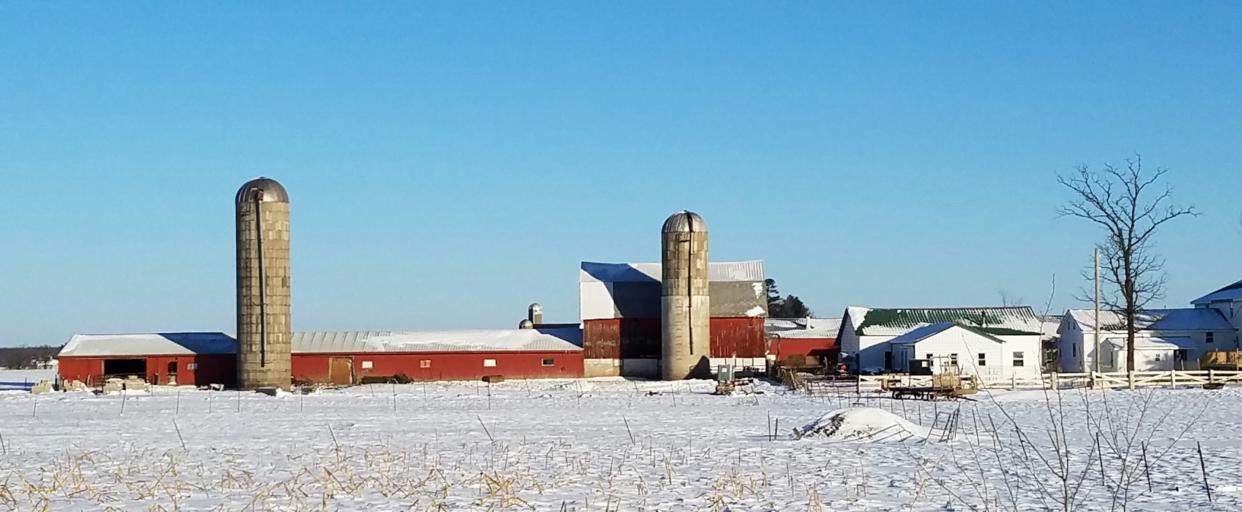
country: US
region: Wisconsin
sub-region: Clark County
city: Loyal
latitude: 44.6404
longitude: -90.3988
